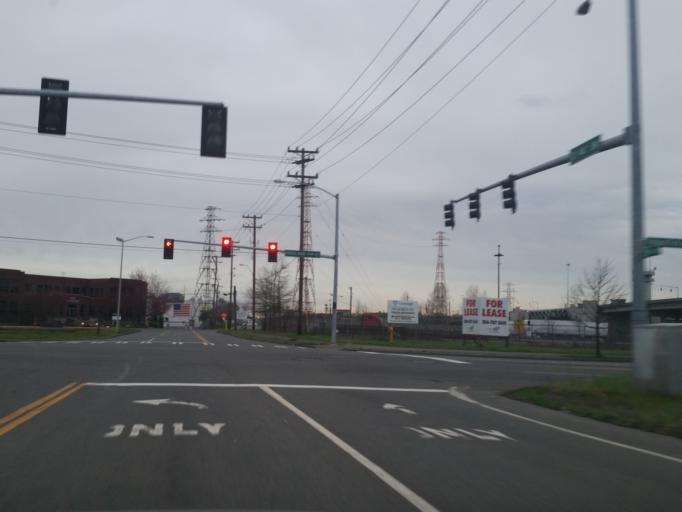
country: US
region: Washington
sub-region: King County
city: White Center
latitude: 47.5395
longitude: -122.3372
